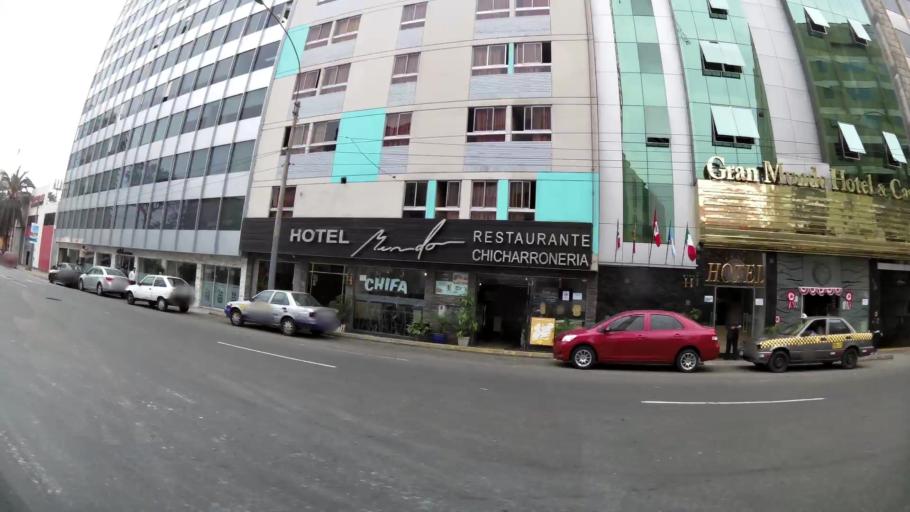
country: PE
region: Lima
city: Lima
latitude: -12.0680
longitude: -77.0382
